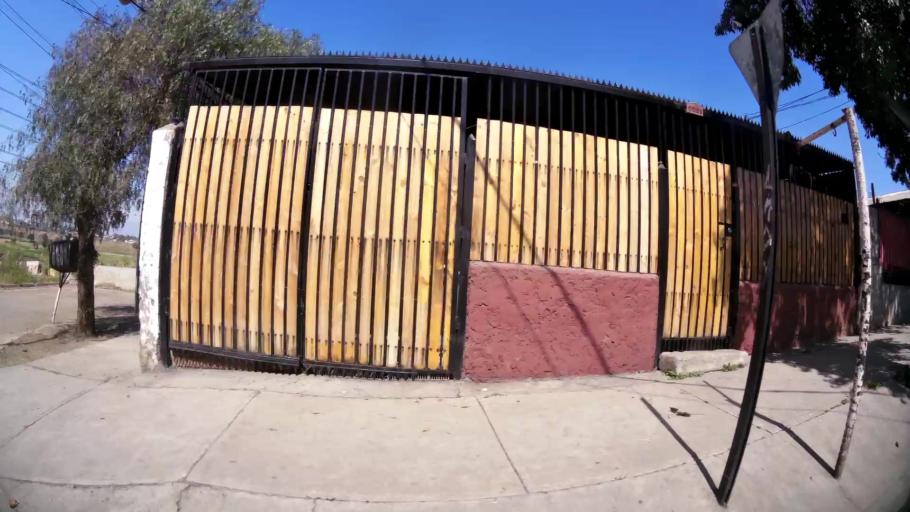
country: CL
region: Santiago Metropolitan
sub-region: Provincia de Santiago
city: Lo Prado
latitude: -33.4904
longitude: -70.7317
